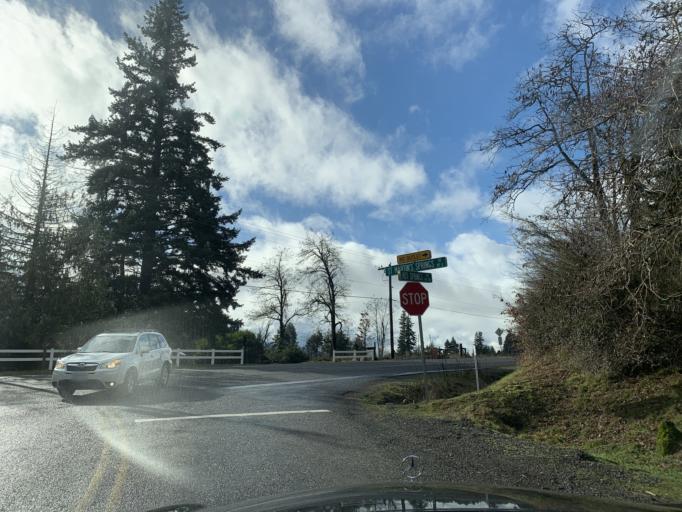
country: US
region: Washington
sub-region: Skamania County
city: Carson
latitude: 45.7263
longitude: -121.8019
